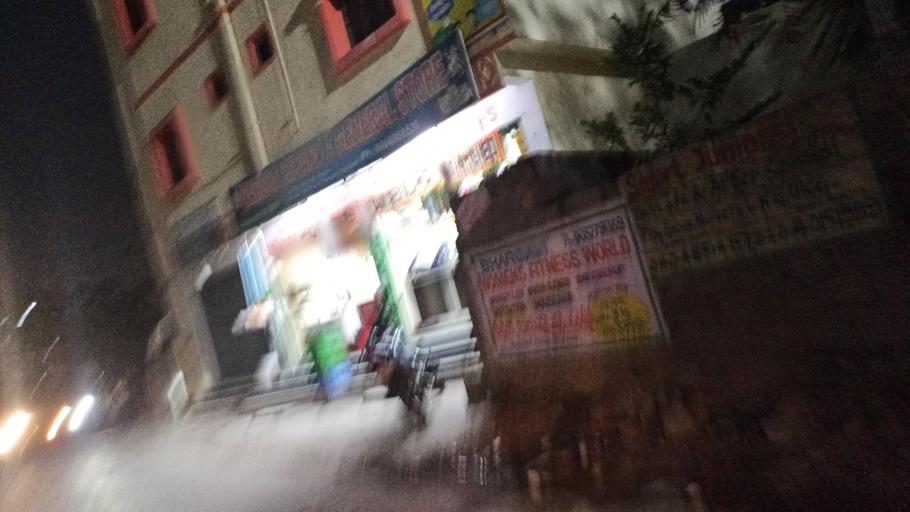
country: IN
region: Telangana
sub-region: Rangareddi
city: Kukatpalli
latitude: 17.5197
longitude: 78.3853
